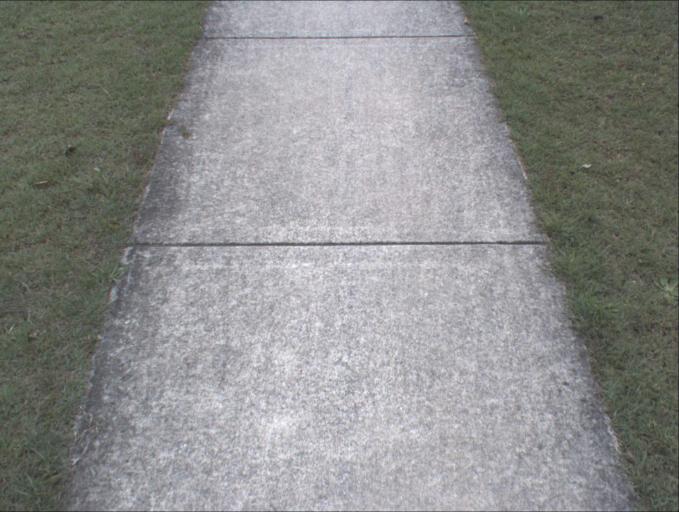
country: AU
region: Queensland
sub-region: Logan
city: Park Ridge South
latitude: -27.6660
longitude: 153.0239
